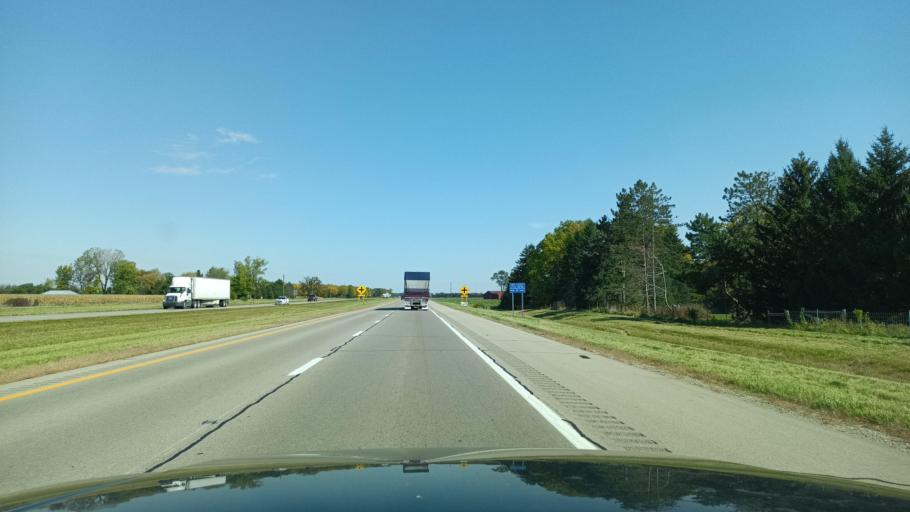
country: US
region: Ohio
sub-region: Henry County
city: Napoleon
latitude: 41.3710
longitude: -84.1946
